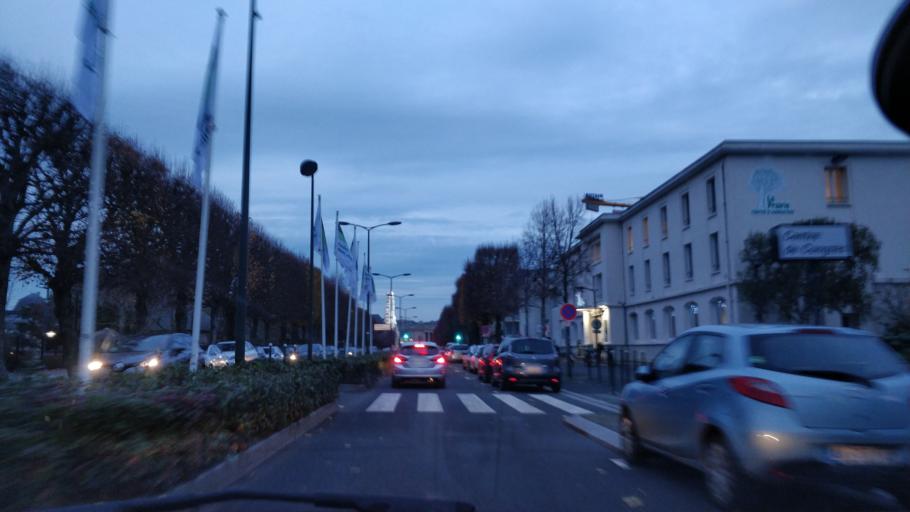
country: FR
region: Lower Normandy
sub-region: Departement du Calvados
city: Caen
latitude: 49.1772
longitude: -0.3710
